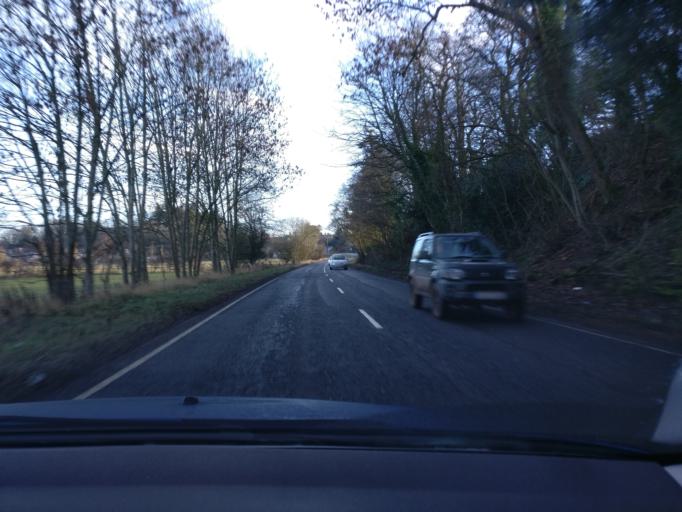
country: GB
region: Scotland
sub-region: The Scottish Borders
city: Hawick
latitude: 55.4561
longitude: -2.6927
